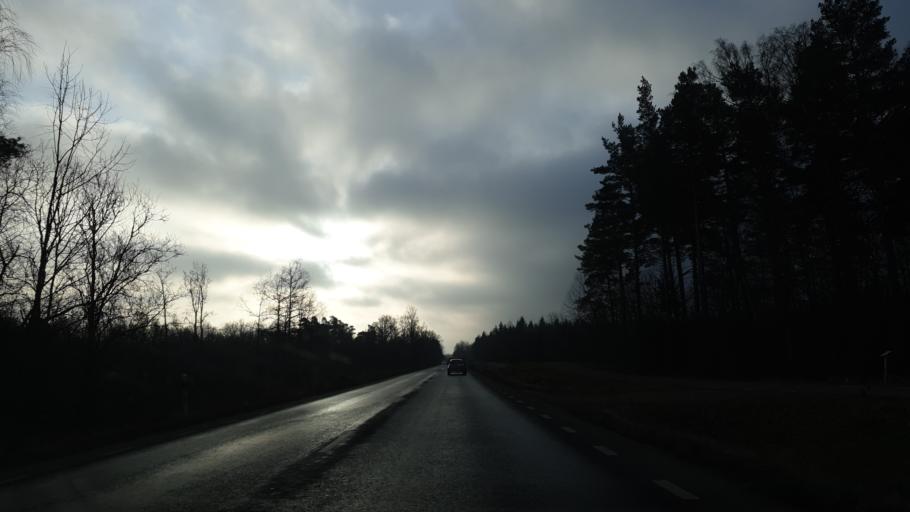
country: SE
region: Blekinge
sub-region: Karlshamns Kommun
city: Morrum
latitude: 56.1445
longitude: 14.6692
